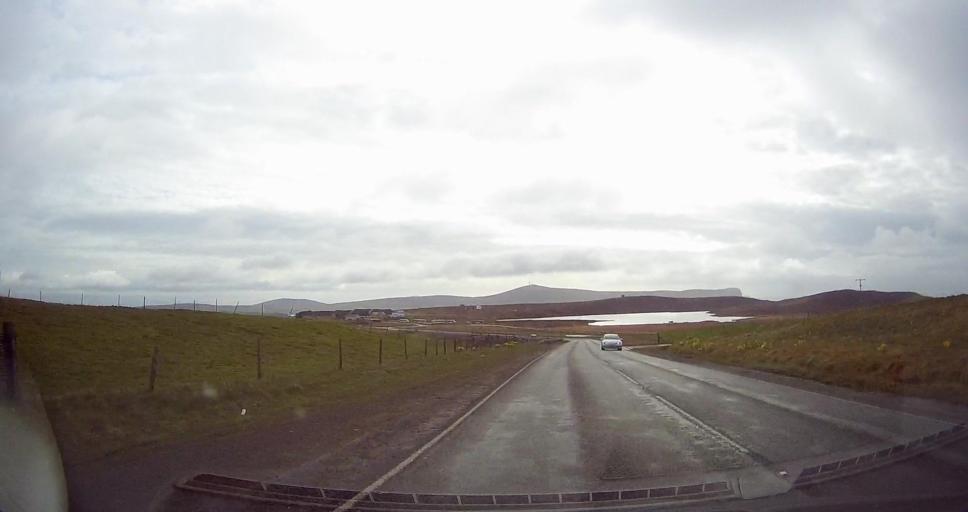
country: GB
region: Scotland
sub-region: Shetland Islands
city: Lerwick
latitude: 60.1389
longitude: -1.1996
